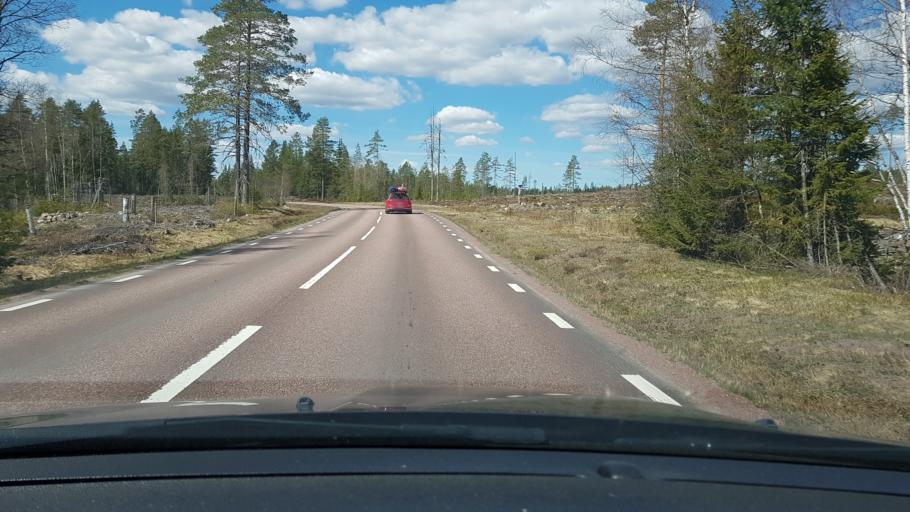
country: SE
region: Dalarna
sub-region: Alvdalens Kommun
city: AElvdalen
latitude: 61.0849
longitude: 13.7650
